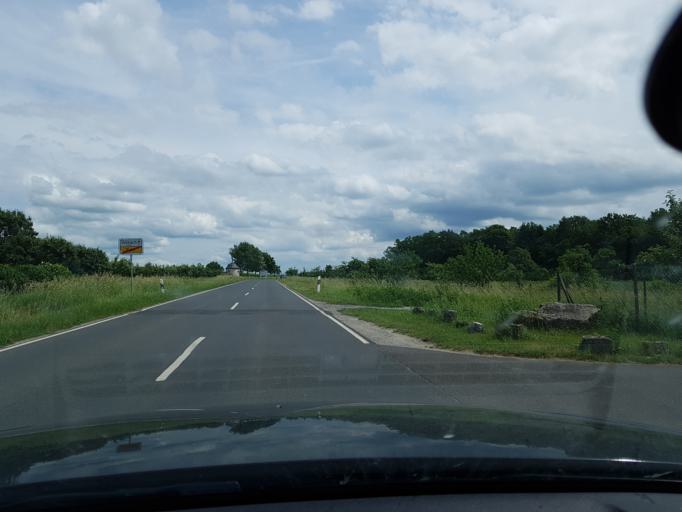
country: DE
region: Bavaria
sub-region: Regierungsbezirk Unterfranken
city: Nordheim
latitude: 49.8763
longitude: 10.1721
